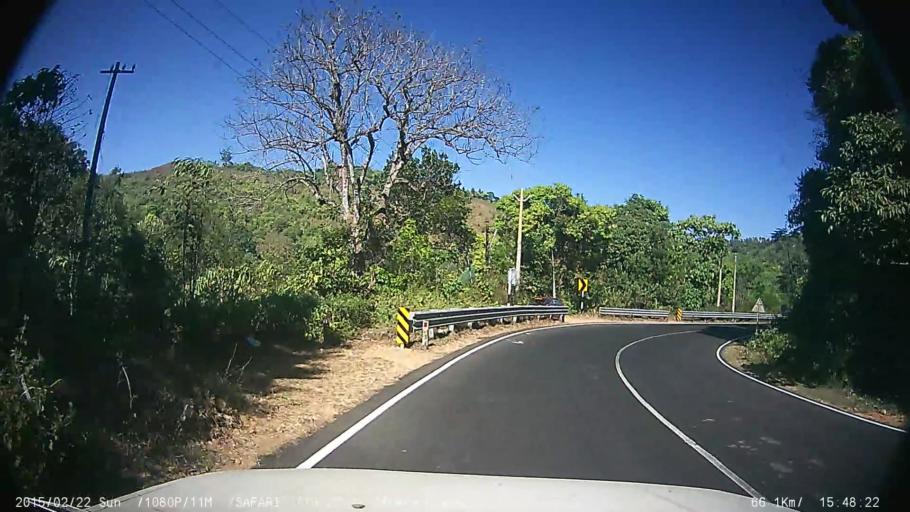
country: IN
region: Kerala
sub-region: Kottayam
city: Erattupetta
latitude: 9.5733
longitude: 76.9925
